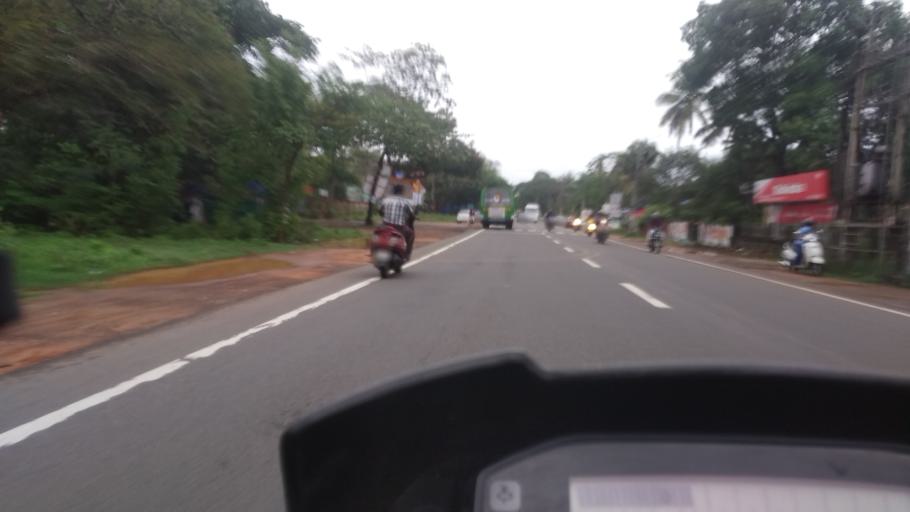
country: IN
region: Kerala
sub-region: Alappuzha
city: Alleppey
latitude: 9.5513
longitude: 76.3274
